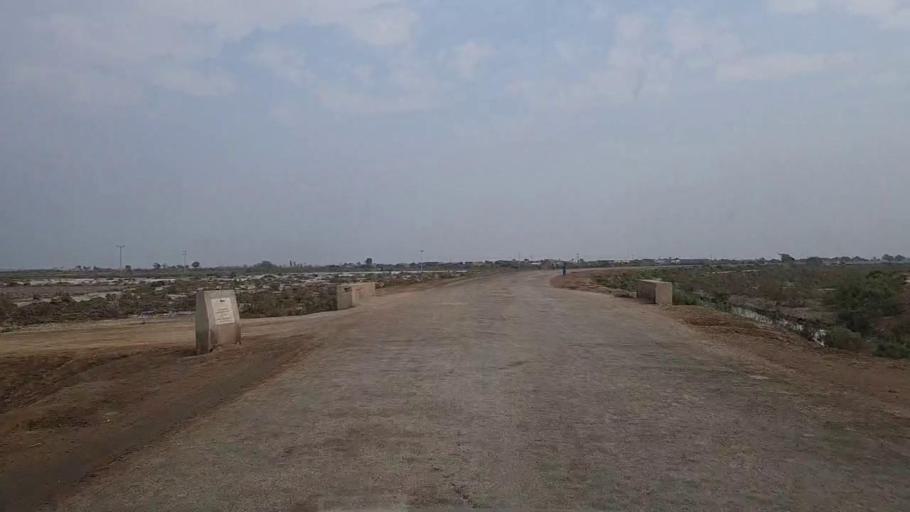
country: PK
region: Sindh
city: Mirwah Gorchani
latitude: 25.3802
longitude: 69.0924
